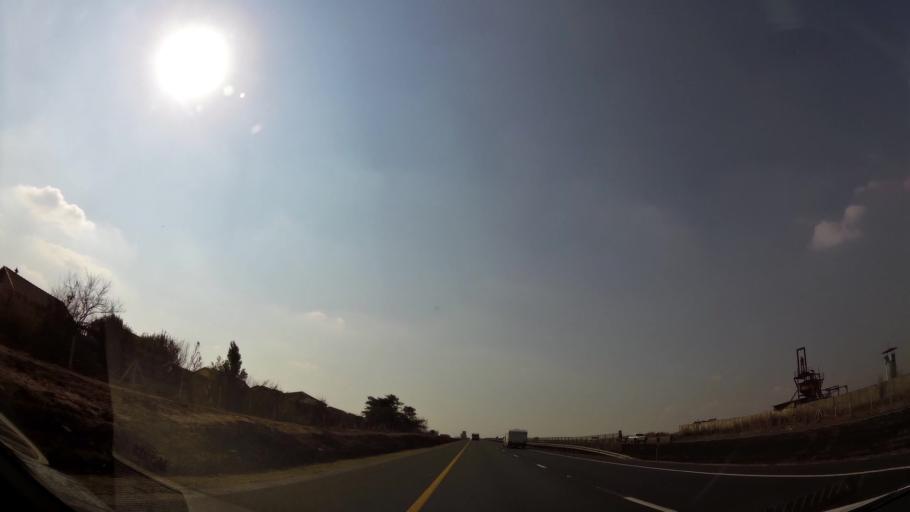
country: ZA
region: Gauteng
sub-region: Ekurhuleni Metropolitan Municipality
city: Brakpan
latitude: -26.1621
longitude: 28.4117
